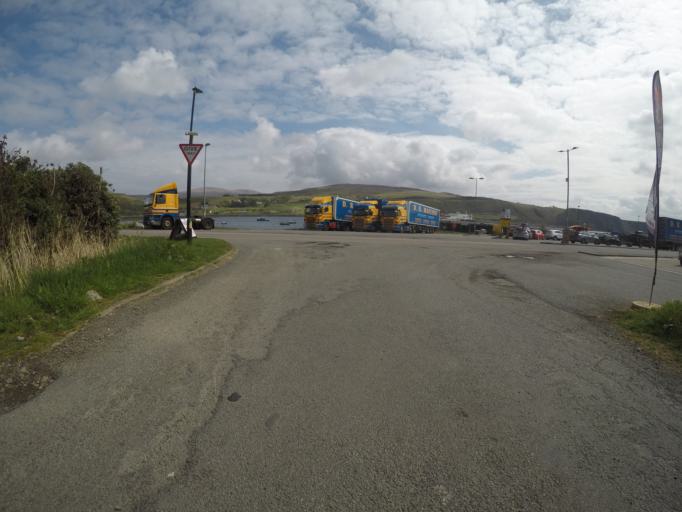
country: GB
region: Scotland
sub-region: Highland
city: Portree
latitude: 57.5876
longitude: -6.3763
